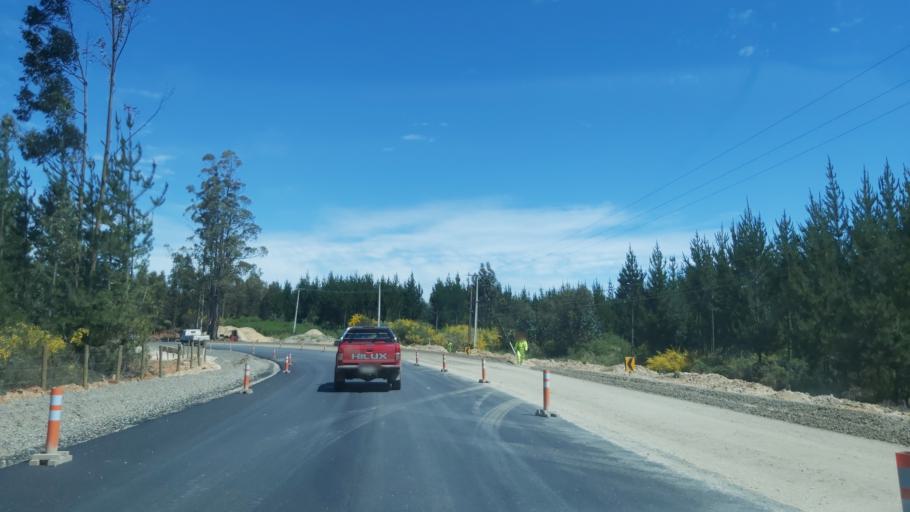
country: CL
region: Maule
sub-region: Provincia de Talca
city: Constitucion
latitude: -35.3827
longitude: -72.4209
